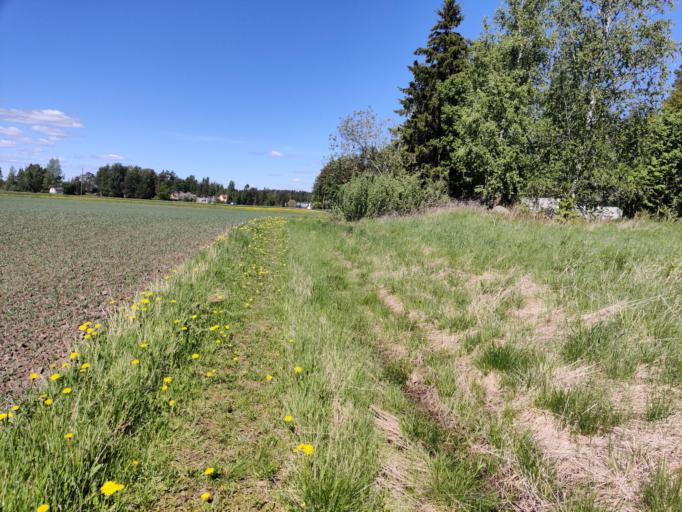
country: FI
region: Paijanne Tavastia
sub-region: Lahti
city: Lahti
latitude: 61.0579
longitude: 25.6729
